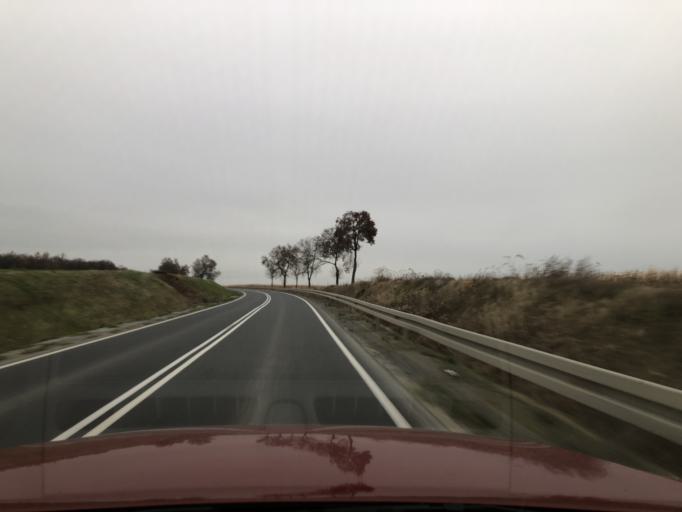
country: PL
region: Lower Silesian Voivodeship
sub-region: Powiat swidnicki
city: Zarow
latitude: 50.9755
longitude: 16.4975
